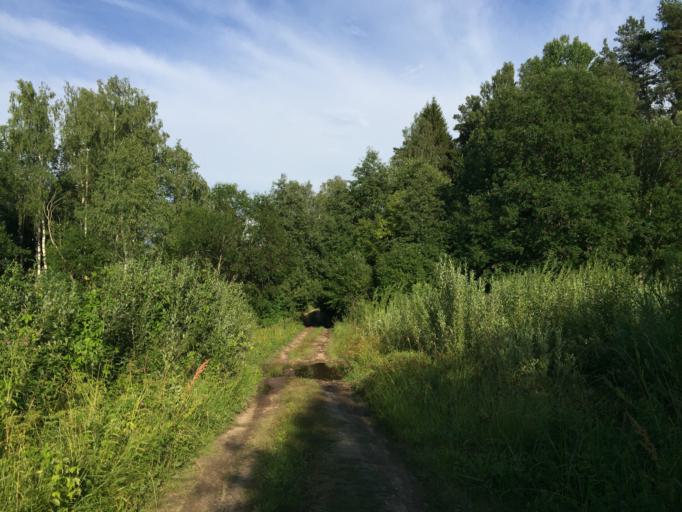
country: LV
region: Krimulda
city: Ragana
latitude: 57.1448
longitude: 24.7617
